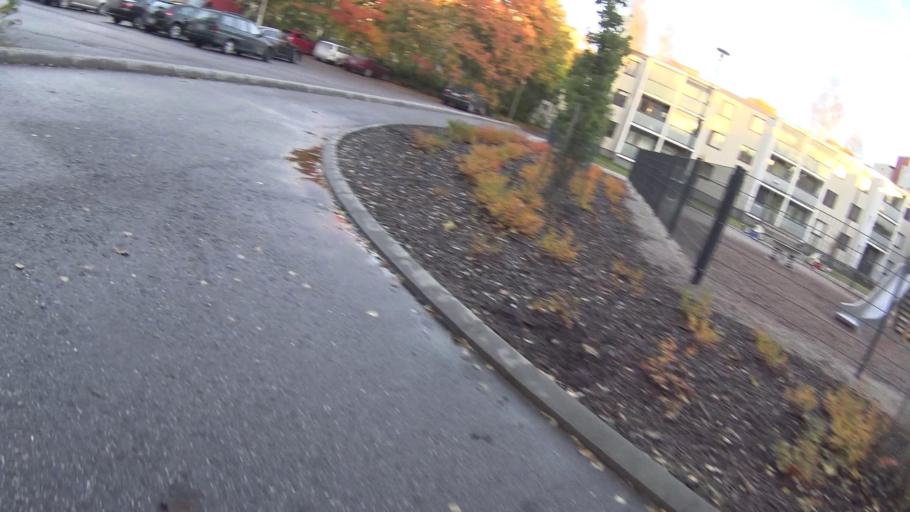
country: FI
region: Uusimaa
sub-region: Helsinki
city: Teekkarikylae
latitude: 60.2162
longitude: 24.8240
